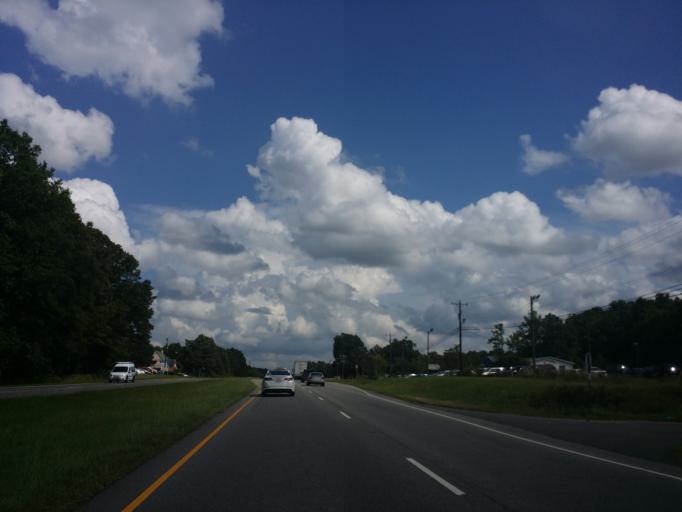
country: US
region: North Carolina
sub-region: Durham County
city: Durham
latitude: 35.9440
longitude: -78.8284
